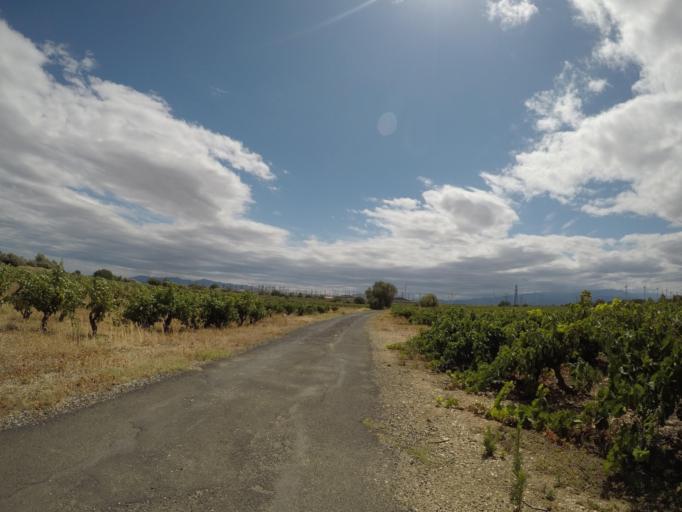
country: FR
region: Languedoc-Roussillon
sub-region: Departement des Pyrenees-Orientales
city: Baixas
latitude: 42.7373
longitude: 2.8029
